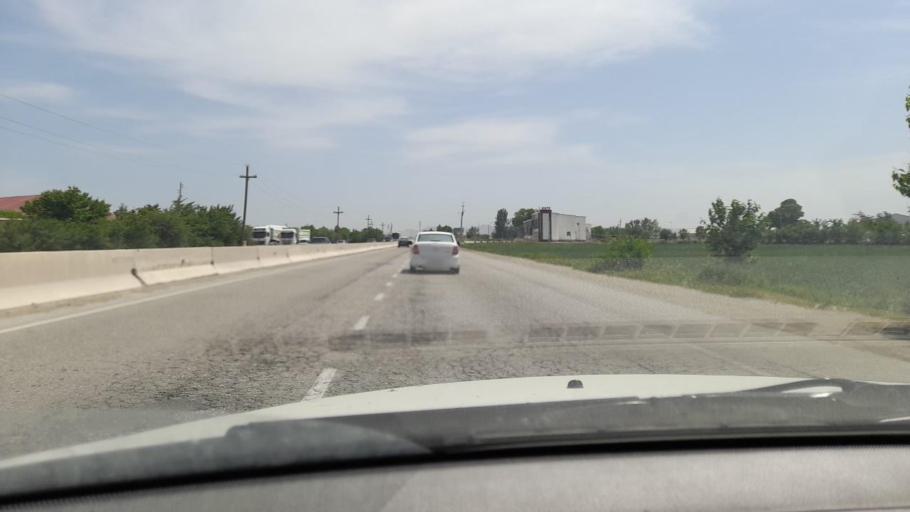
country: UZ
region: Navoiy
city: Karmana Shahri
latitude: 40.1342
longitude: 65.4056
